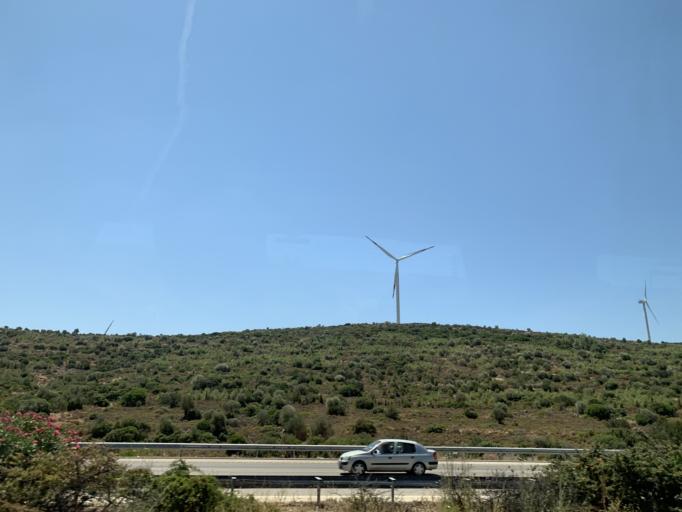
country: TR
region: Izmir
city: Uzunkuyu
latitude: 38.2690
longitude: 26.4836
